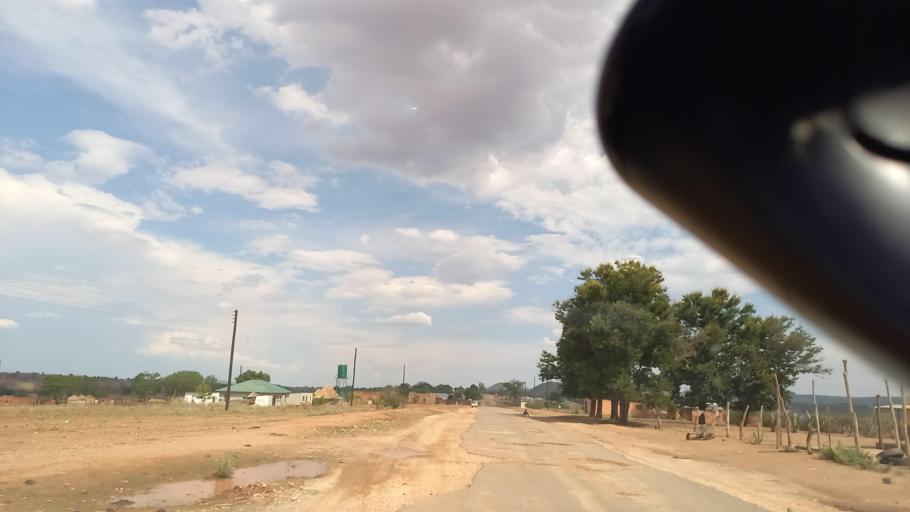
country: ZM
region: Lusaka
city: Kafue
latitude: -16.2209
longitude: 28.1239
